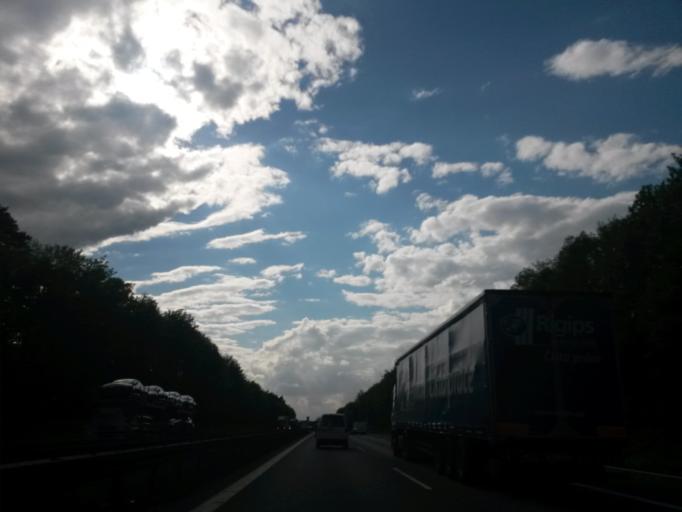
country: DE
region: Bavaria
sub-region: Regierungsbezirk Mittelfranken
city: Neuendettelsau
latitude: 49.3052
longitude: 10.7873
